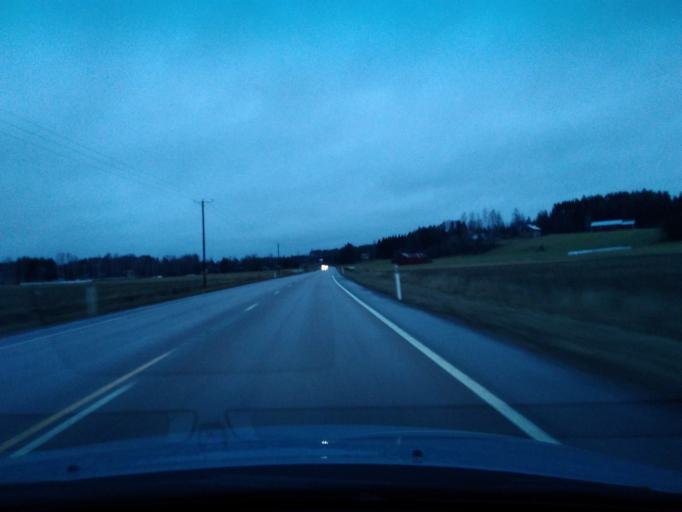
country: FI
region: Uusimaa
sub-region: Porvoo
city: Askola
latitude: 60.4547
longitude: 25.5822
